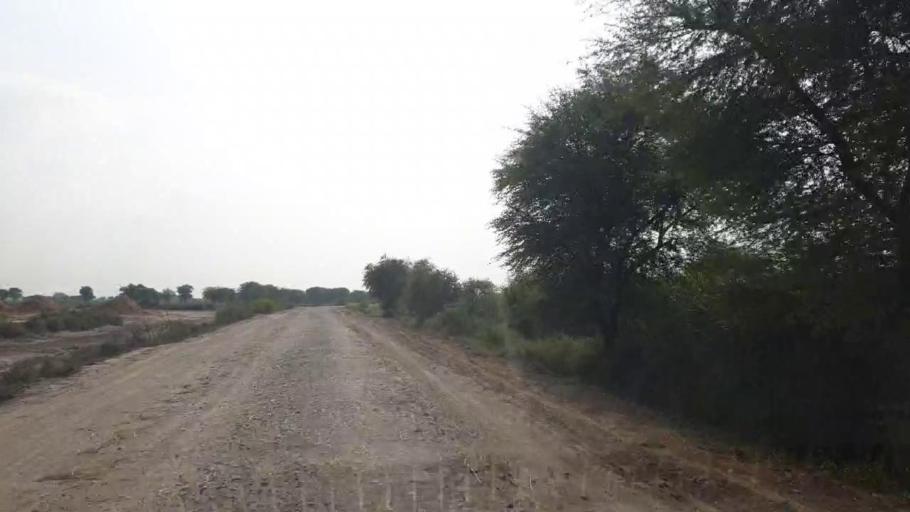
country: PK
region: Sindh
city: Rajo Khanani
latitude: 25.0288
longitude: 68.8046
